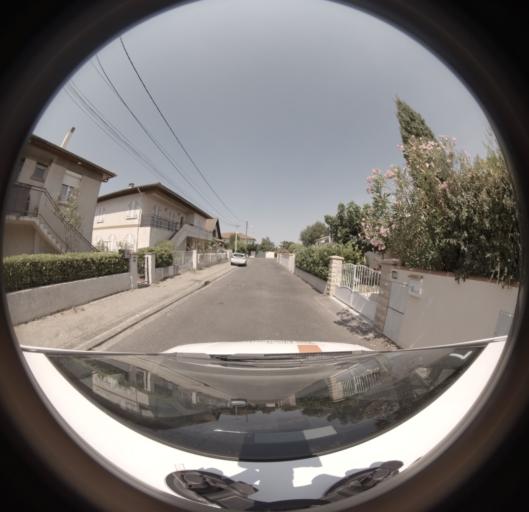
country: FR
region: Midi-Pyrenees
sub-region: Departement du Tarn-et-Garonne
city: Montauban
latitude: 44.0206
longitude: 1.3713
